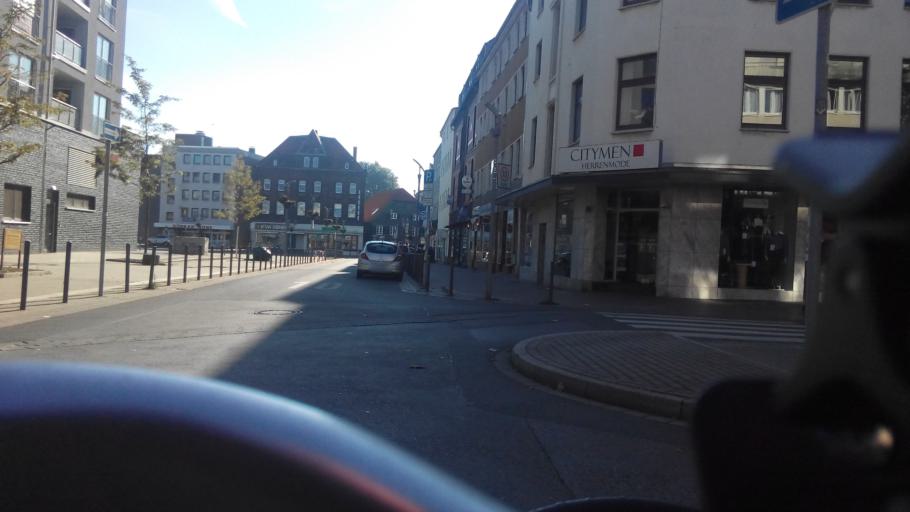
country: DE
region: North Rhine-Westphalia
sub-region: Regierungsbezirk Munster
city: Gelsenkirchen
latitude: 51.5127
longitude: 7.0954
